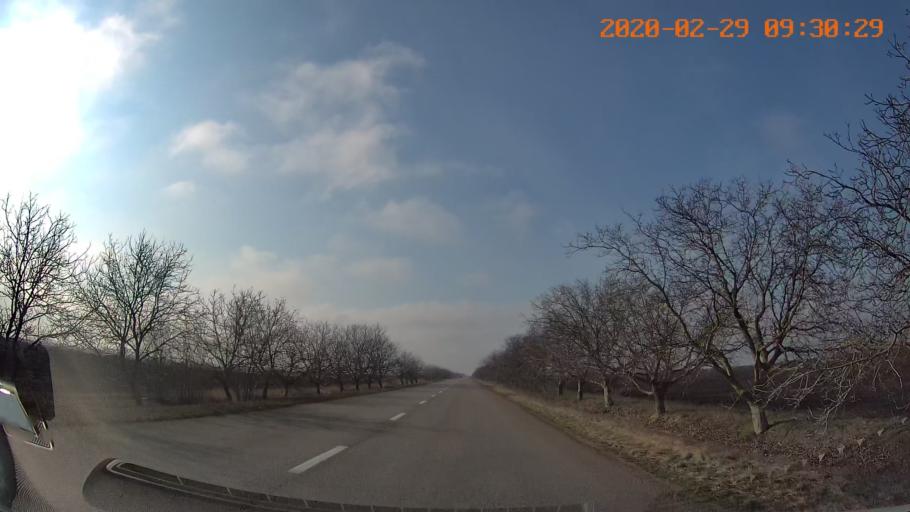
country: MD
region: Telenesti
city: Dnestrovsc
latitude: 46.6658
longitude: 29.9163
